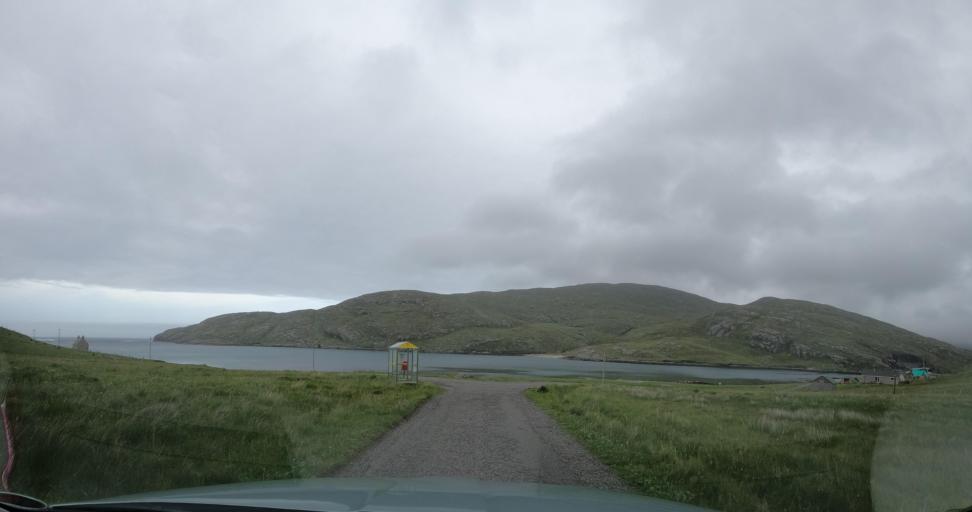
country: GB
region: Scotland
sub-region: Eilean Siar
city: Barra
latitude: 56.9432
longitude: -7.5435
